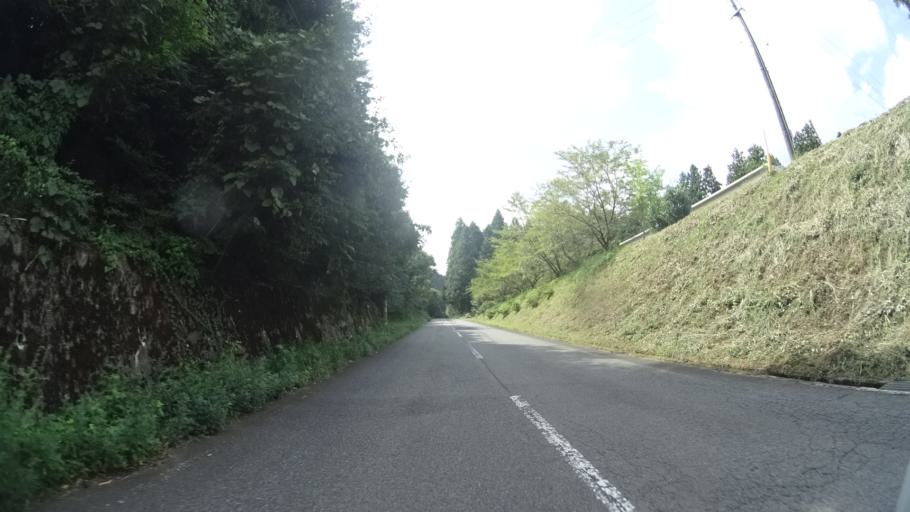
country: JP
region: Yamaguchi
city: Hagi
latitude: 34.5118
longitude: 131.5933
